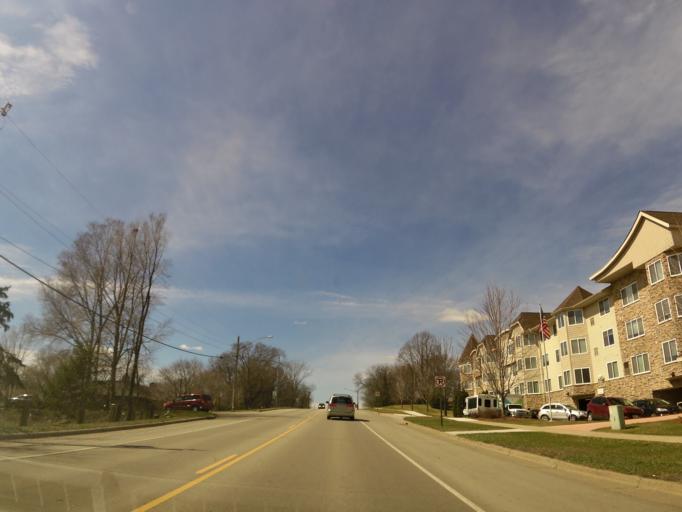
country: US
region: Minnesota
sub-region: Goodhue County
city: Cannon Falls
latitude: 44.5069
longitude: -92.9123
